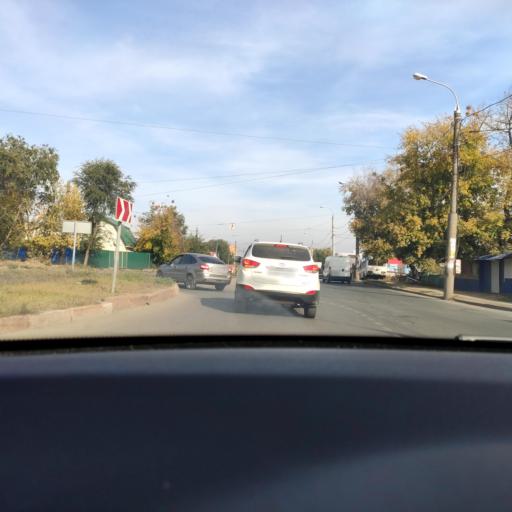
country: RU
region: Samara
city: Samara
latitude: 53.1920
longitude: 50.2132
